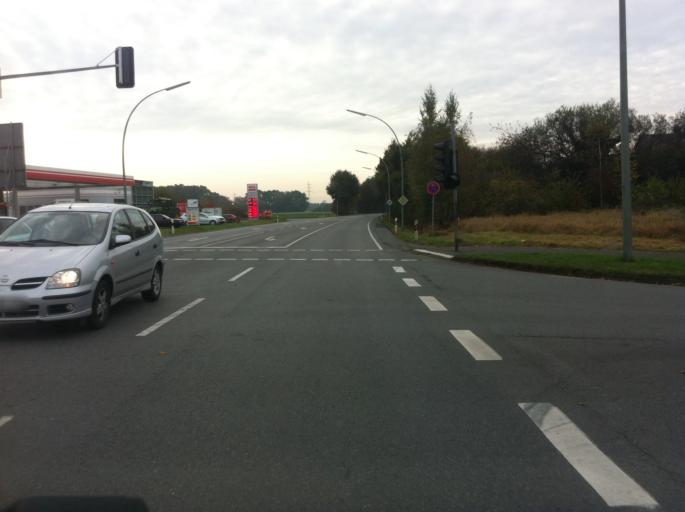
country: DE
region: North Rhine-Westphalia
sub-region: Regierungsbezirk Munster
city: Vreden
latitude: 52.0346
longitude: 6.8411
